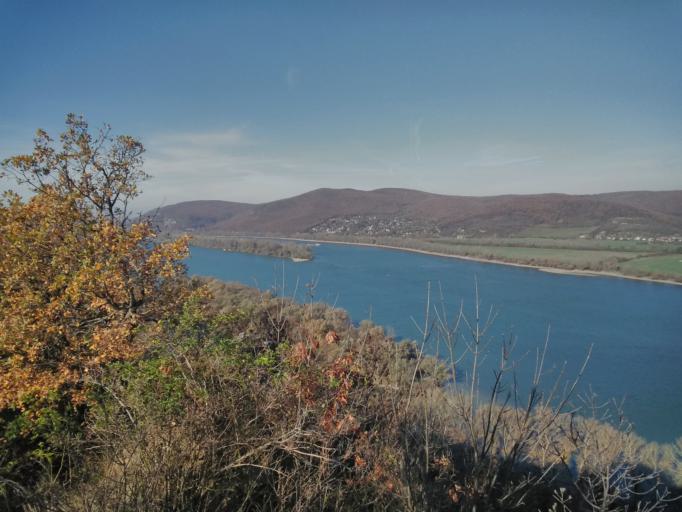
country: HU
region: Pest
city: Szob
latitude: 47.8131
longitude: 18.8211
